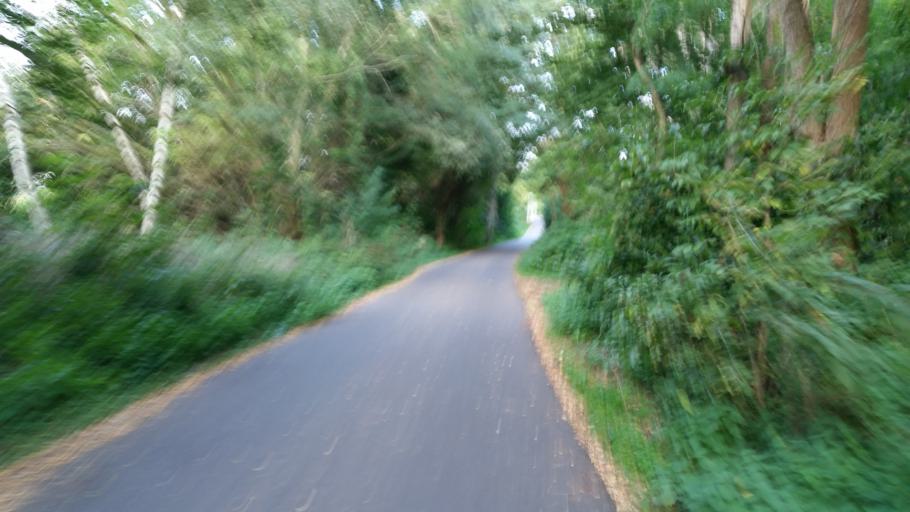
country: DE
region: Brandenburg
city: Teltow
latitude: 52.4036
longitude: 13.2709
